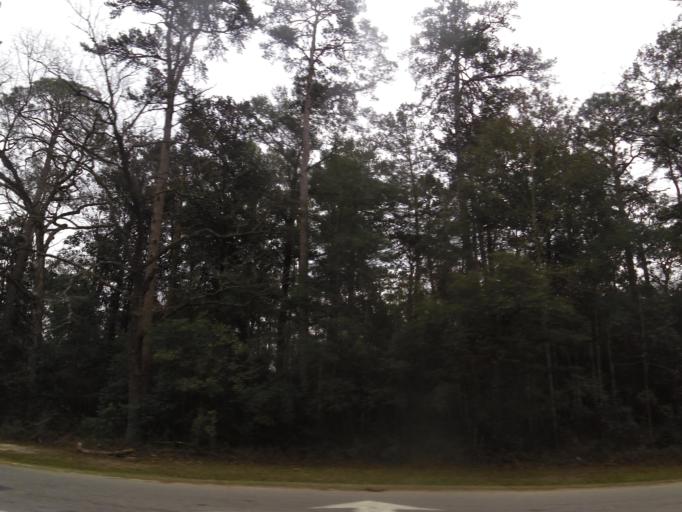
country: US
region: Georgia
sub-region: Thomas County
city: Thomasville
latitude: 30.8159
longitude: -83.9484
